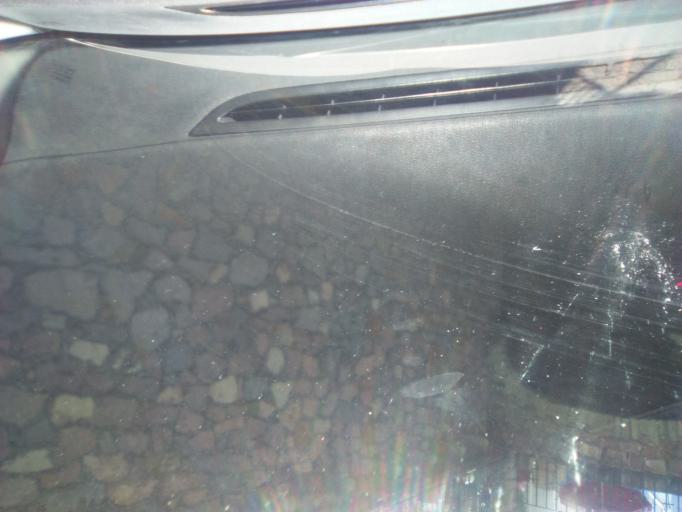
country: MX
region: Guanajuato
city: Guanajuato
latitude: 21.0192
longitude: -101.2588
